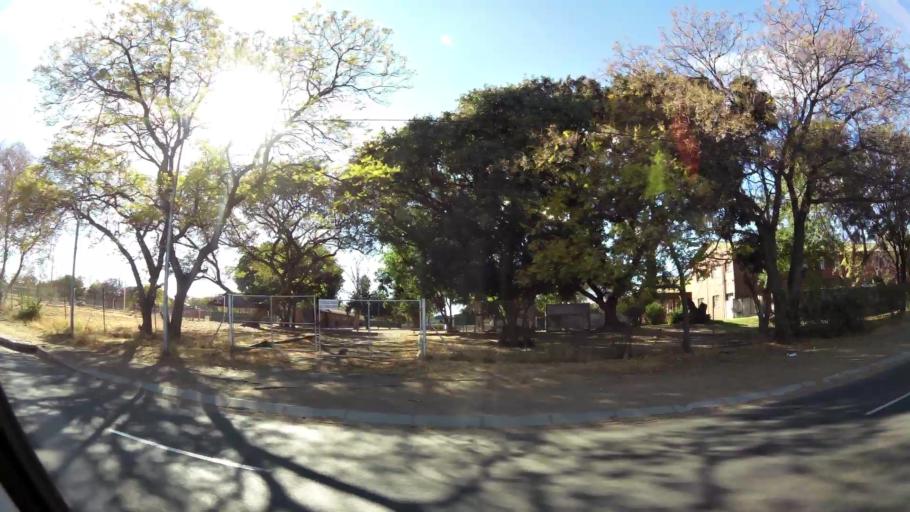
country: ZA
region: Limpopo
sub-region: Capricorn District Municipality
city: Polokwane
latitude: -23.8984
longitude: 29.4538
